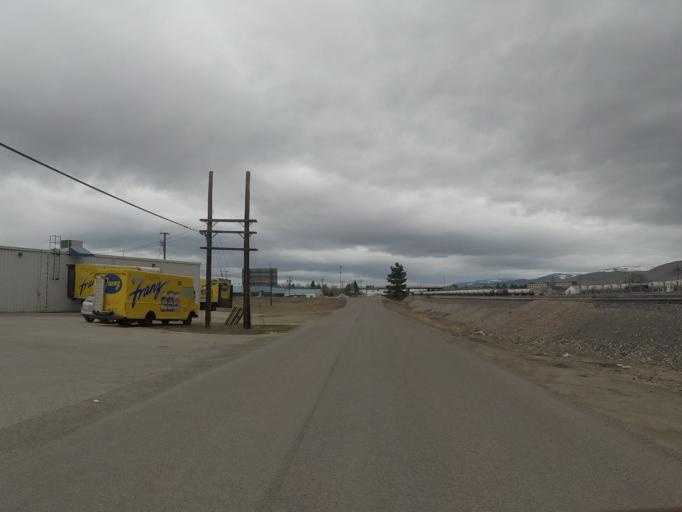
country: US
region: Montana
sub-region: Missoula County
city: Orchard Homes
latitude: 46.8950
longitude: -114.0316
